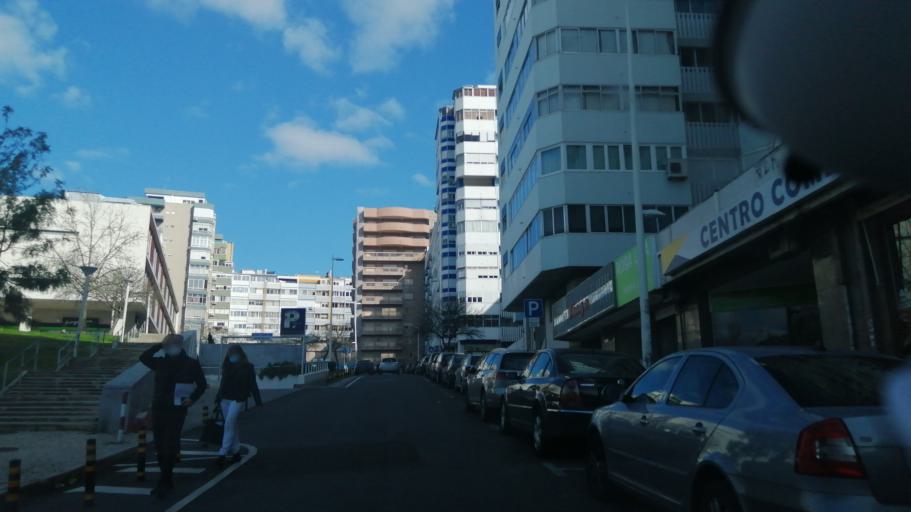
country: PT
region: Setubal
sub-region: Almada
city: Almada
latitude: 38.6779
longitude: -9.1558
